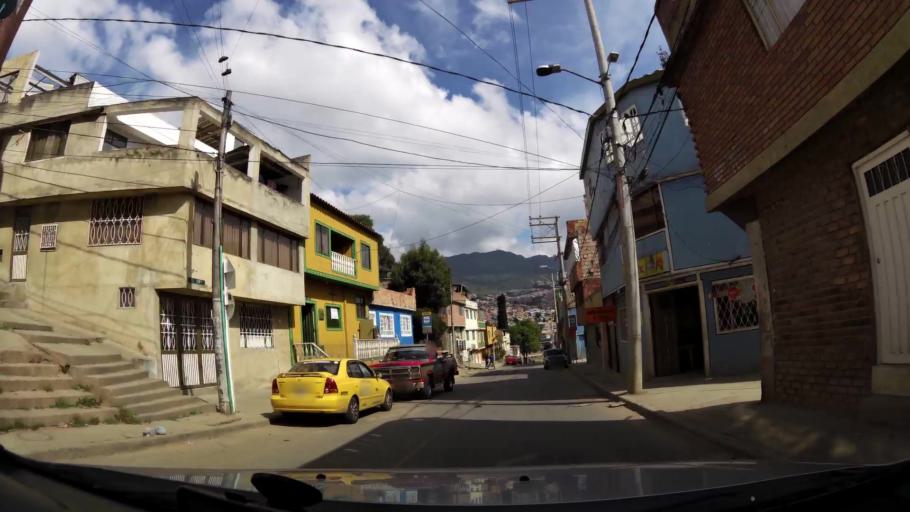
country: CO
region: Bogota D.C.
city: Bogota
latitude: 4.5551
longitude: -74.0973
